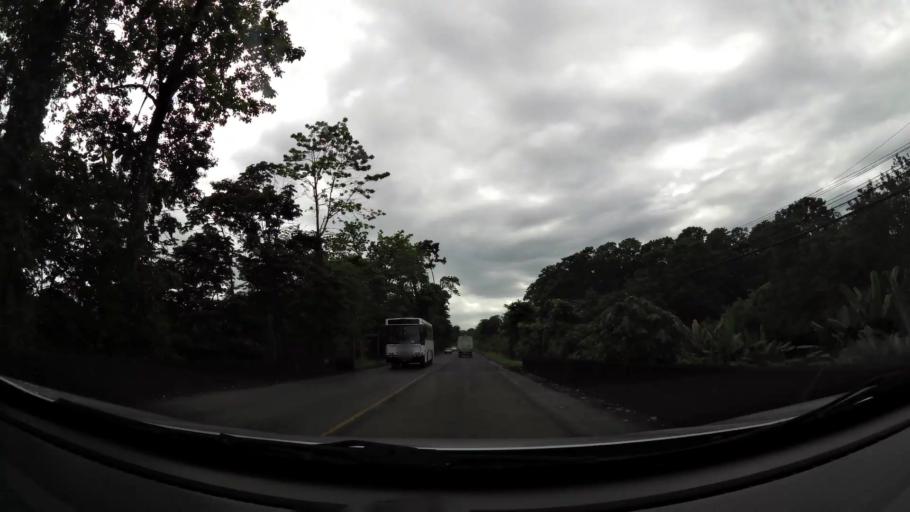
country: CR
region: Limon
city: Pocora
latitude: 10.1622
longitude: -83.6006
